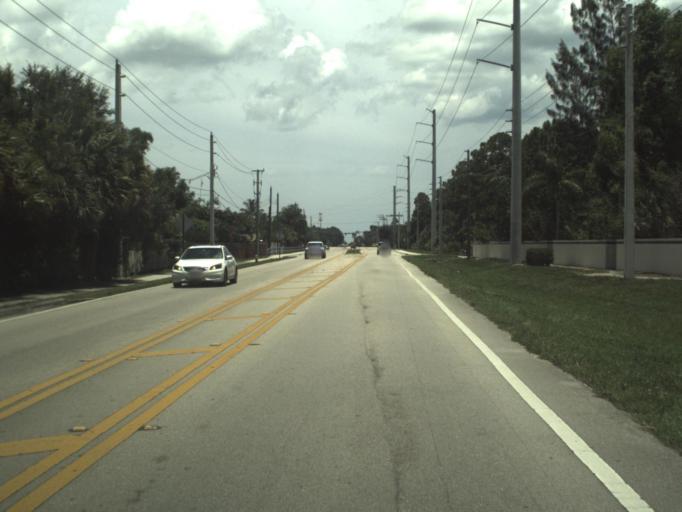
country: US
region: Florida
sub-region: Martin County
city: Port Salerno
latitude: 27.1323
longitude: -80.2111
